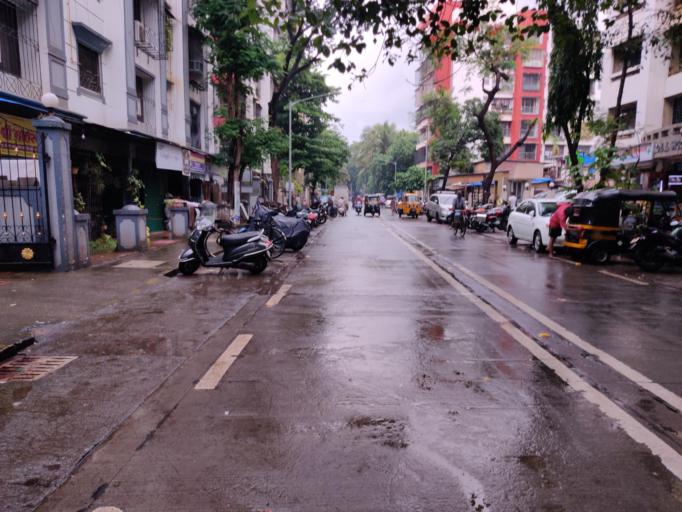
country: IN
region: Maharashtra
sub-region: Mumbai Suburban
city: Borivli
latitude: 19.2501
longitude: 72.8549
